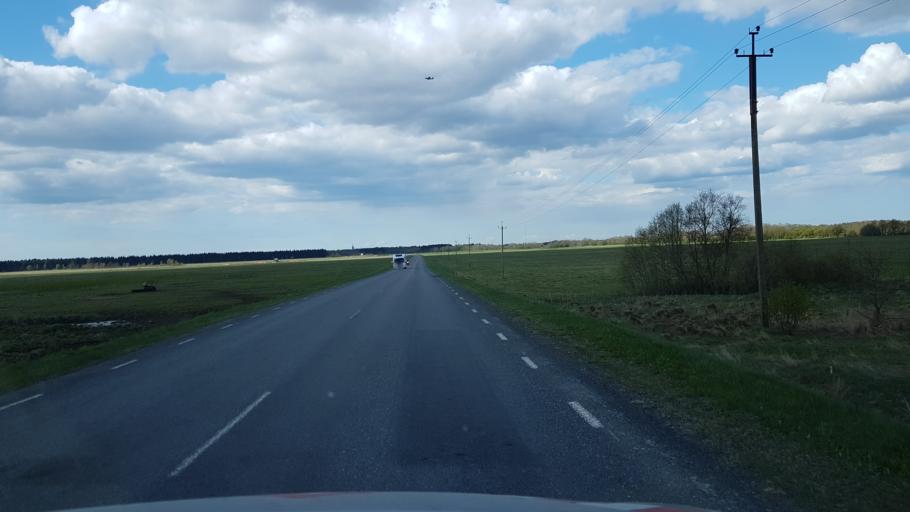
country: EE
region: Harju
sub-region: Keila linn
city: Keila
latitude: 59.2783
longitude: 24.4511
